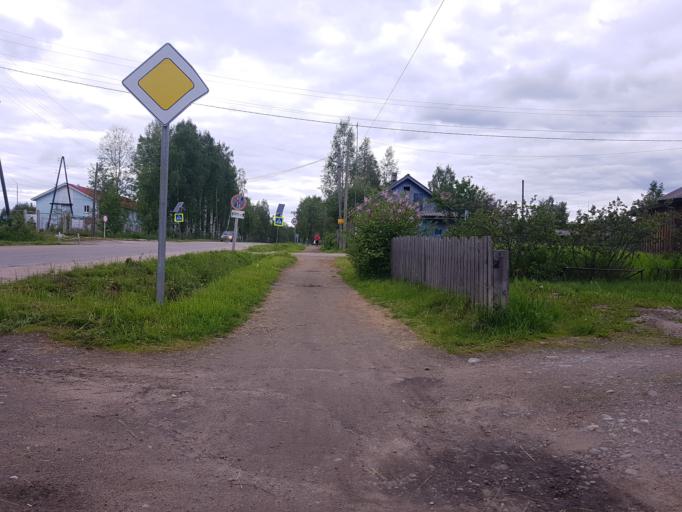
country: RU
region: Republic of Karelia
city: Kalevala
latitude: 65.2014
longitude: 31.1765
